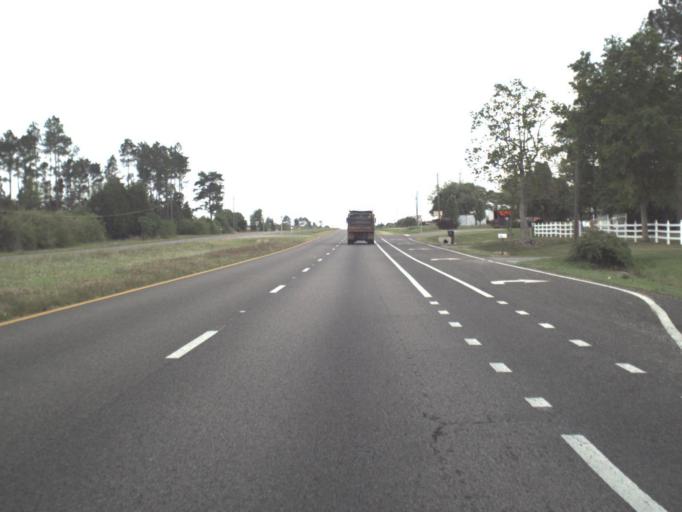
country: US
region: Florida
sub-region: Escambia County
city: Molino
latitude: 30.7051
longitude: -87.3504
